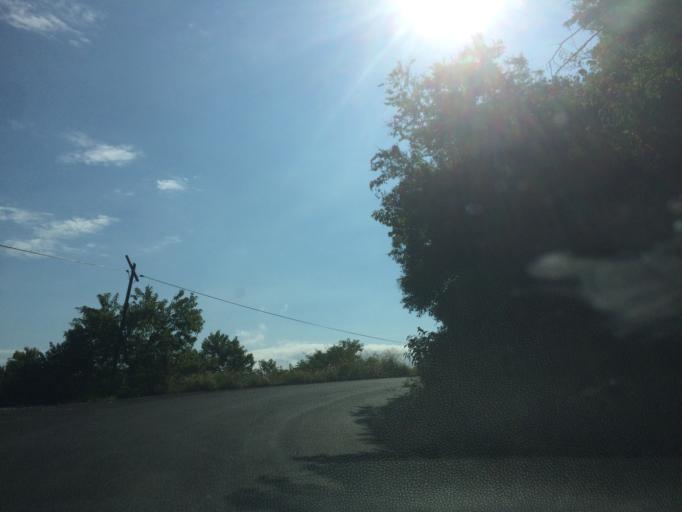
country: MX
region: Nayarit
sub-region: Ahuacatlan
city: Ahuacatlan
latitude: 21.0258
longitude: -104.4748
